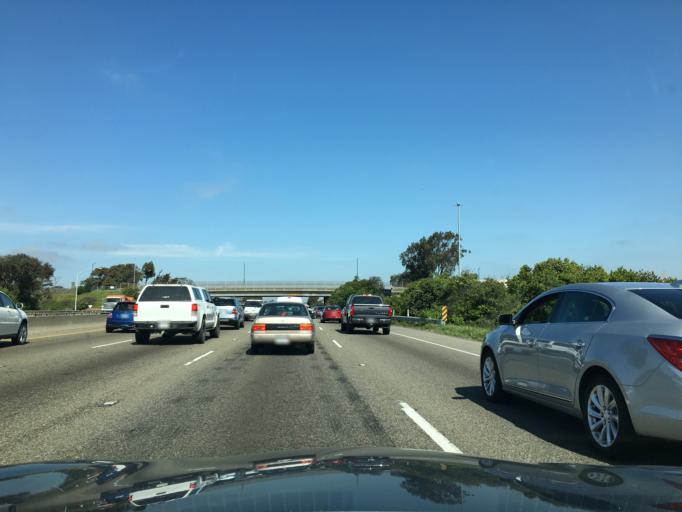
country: US
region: California
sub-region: Alameda County
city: Alameda
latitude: 37.7526
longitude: -122.2068
